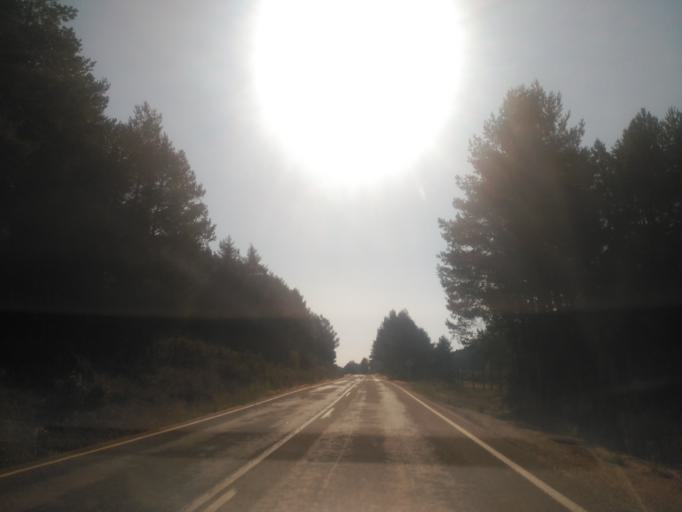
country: ES
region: Castille and Leon
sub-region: Provincia de Soria
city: San Leonardo de Yague
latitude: 41.8137
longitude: -3.0649
